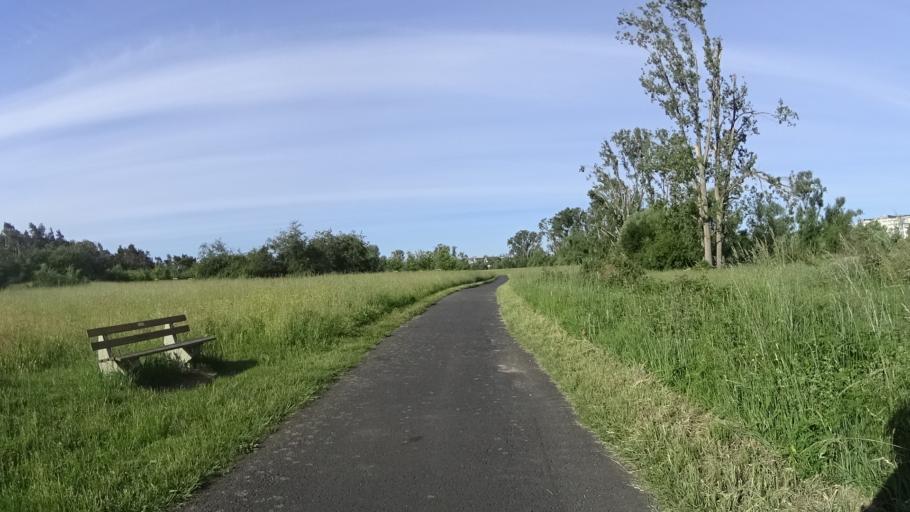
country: DE
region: Hesse
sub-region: Regierungsbezirk Darmstadt
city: Seligenstadt
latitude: 50.0551
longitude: 8.9827
